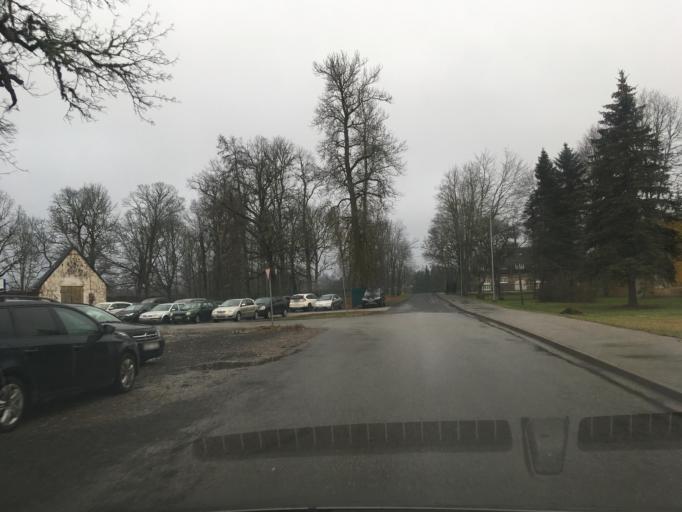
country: EE
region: Tartu
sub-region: Alatskivi vald
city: Kallaste
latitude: 58.3807
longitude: 27.0454
